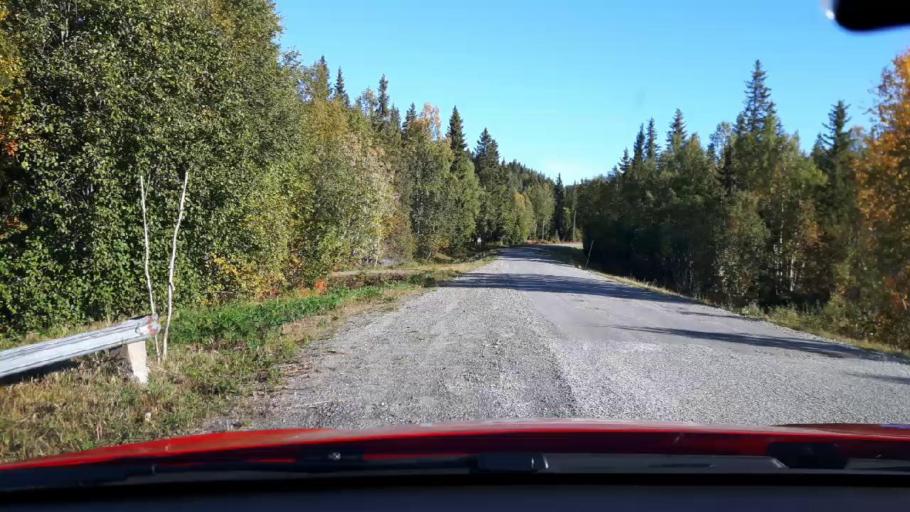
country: NO
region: Nord-Trondelag
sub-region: Lierne
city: Sandvika
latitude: 64.6449
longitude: 13.7355
